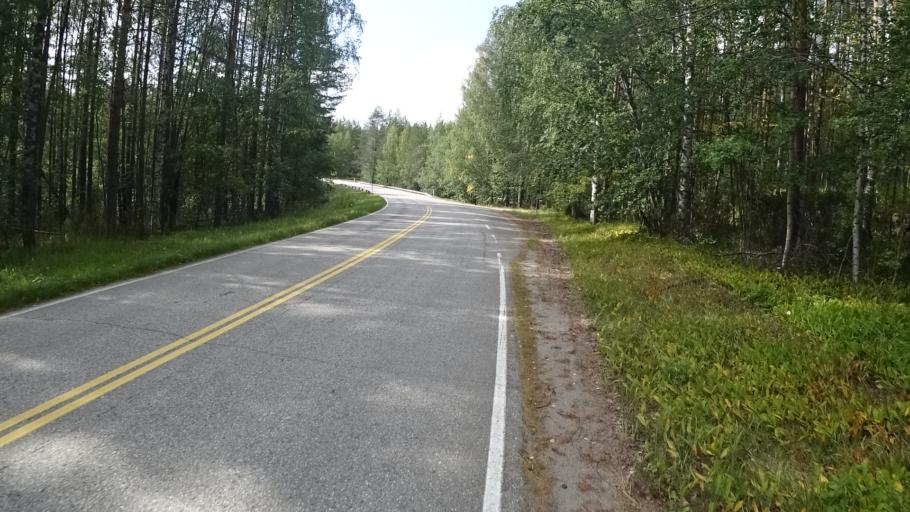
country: FI
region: North Karelia
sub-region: Joensuu
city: Ilomantsi
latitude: 62.6229
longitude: 31.1957
